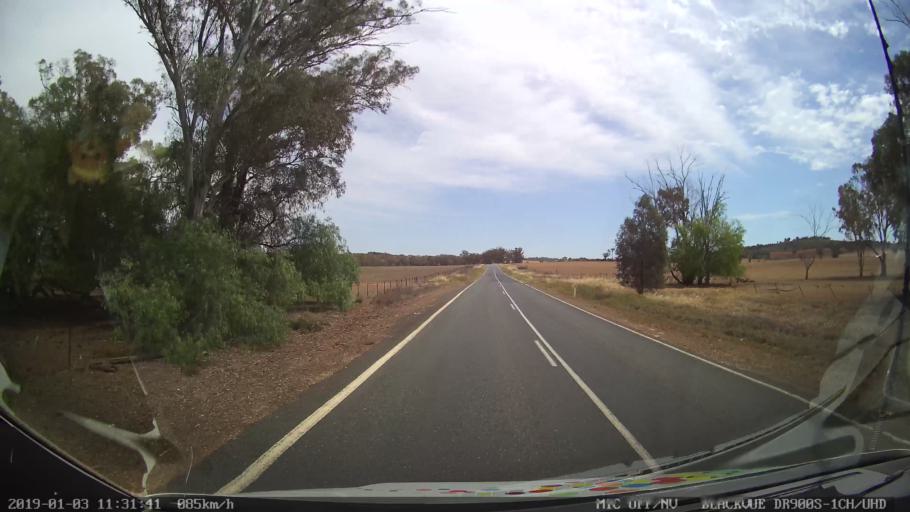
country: AU
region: New South Wales
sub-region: Weddin
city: Grenfell
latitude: -33.9676
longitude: 148.1820
